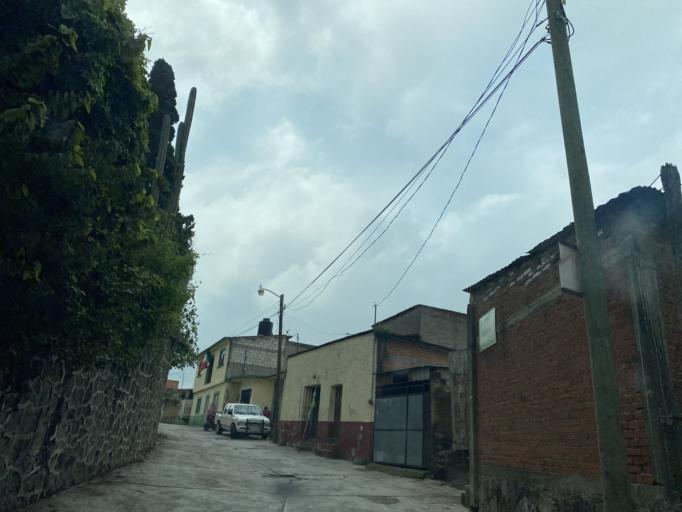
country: MX
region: Morelos
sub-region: Yecapixtla
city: Achichipico
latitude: 18.9503
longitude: -98.8281
